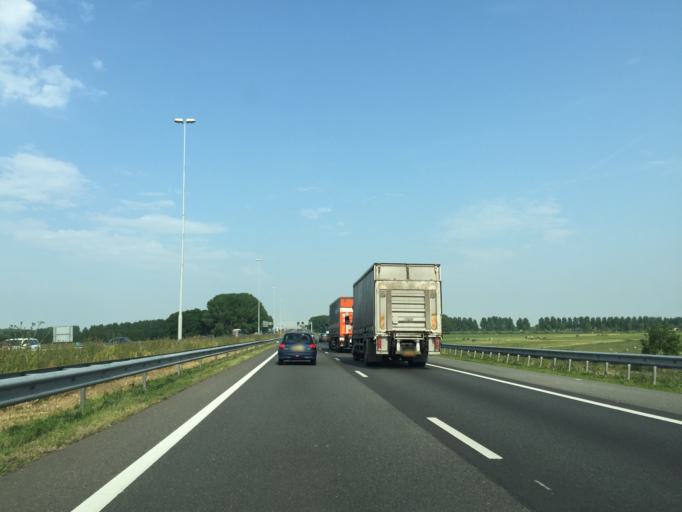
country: NL
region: Utrecht
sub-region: Gemeente Vianen
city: Vianen
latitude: 51.9555
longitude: 5.0417
